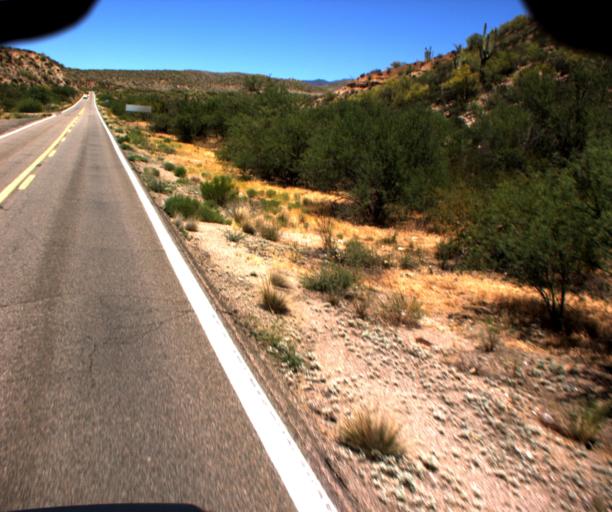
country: US
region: Arizona
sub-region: Pinal County
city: Kearny
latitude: 33.1479
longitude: -110.8011
